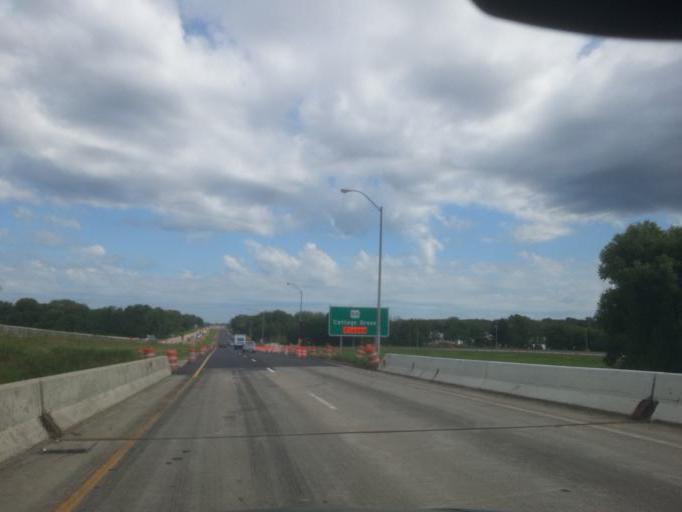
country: US
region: Wisconsin
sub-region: Dane County
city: Monona
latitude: 43.0840
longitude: -89.3111
